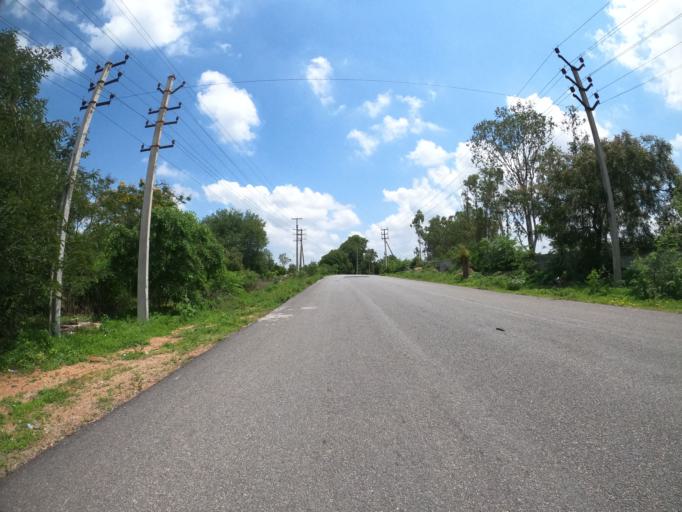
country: IN
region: Telangana
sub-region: Medak
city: Serilingampalle
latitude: 17.3933
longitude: 78.3132
